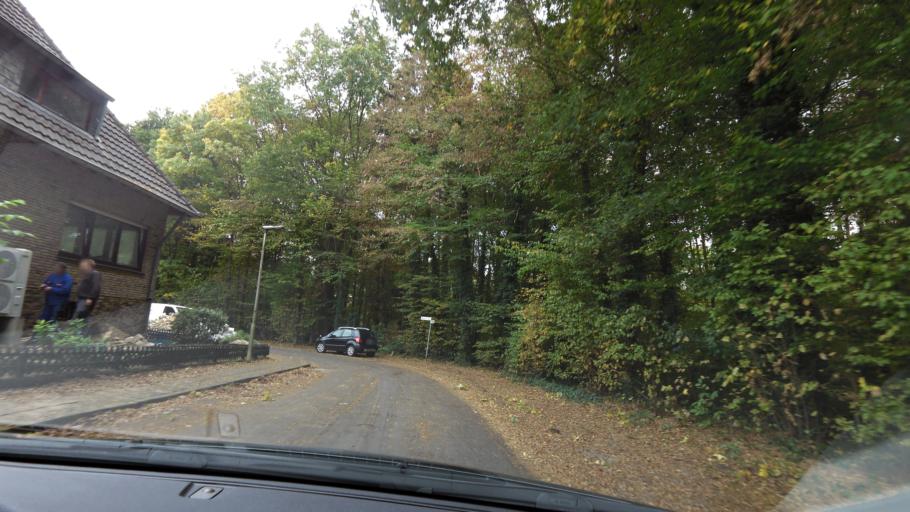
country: DE
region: North Rhine-Westphalia
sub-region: Regierungsbezirk Koln
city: Gangelt
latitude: 50.9873
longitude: 6.0010
